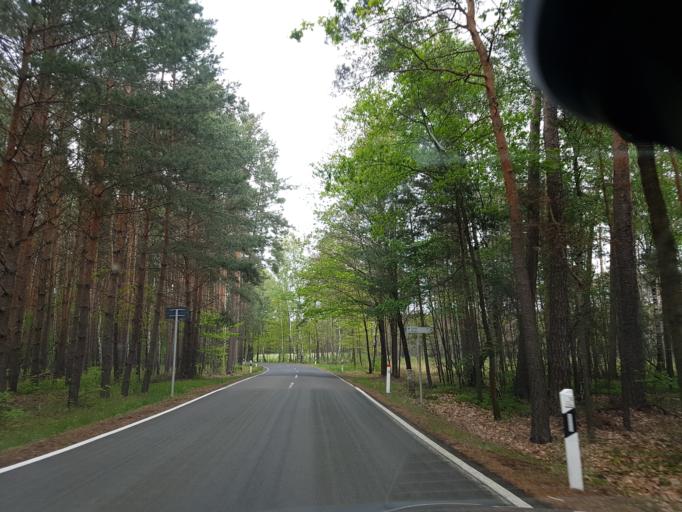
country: DE
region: Brandenburg
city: Crinitz
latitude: 51.7540
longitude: 13.7523
